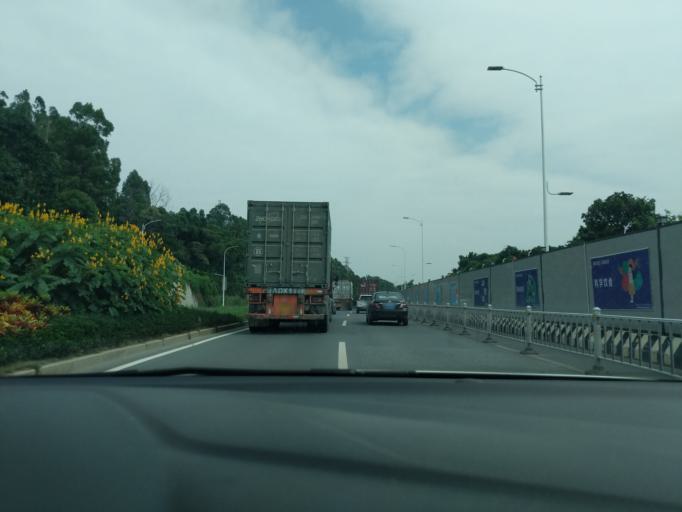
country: CN
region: Guangdong
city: Nansha
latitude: 22.7550
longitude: 113.5726
